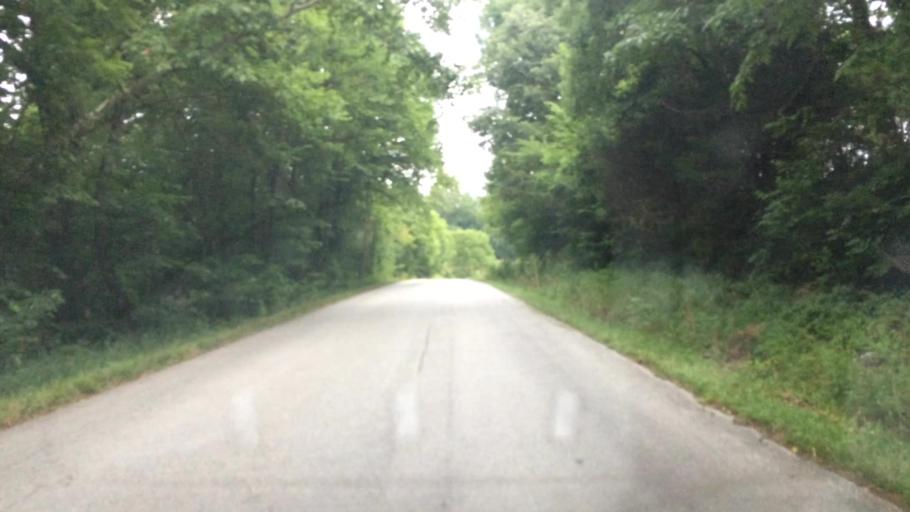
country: US
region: Missouri
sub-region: Greene County
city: Strafford
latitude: 37.3116
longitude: -93.0698
